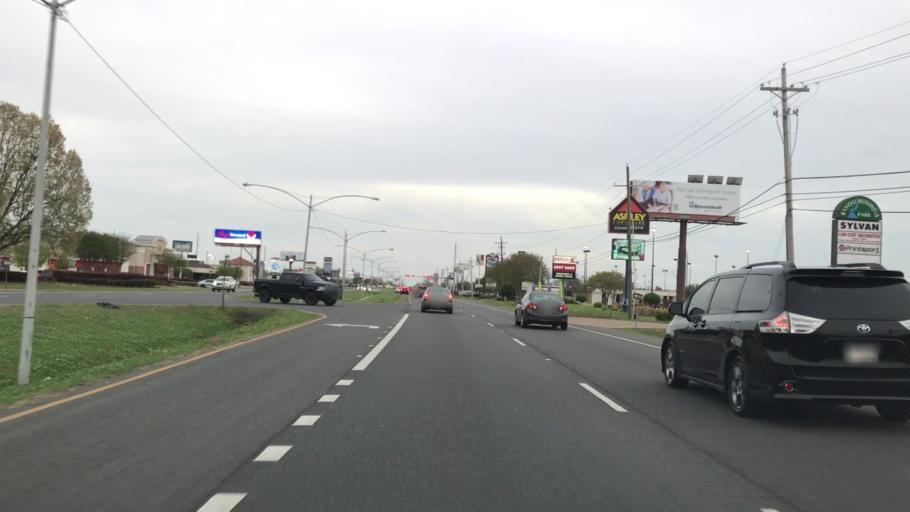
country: US
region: Louisiana
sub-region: Bossier Parish
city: Bossier City
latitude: 32.4478
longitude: -93.7212
